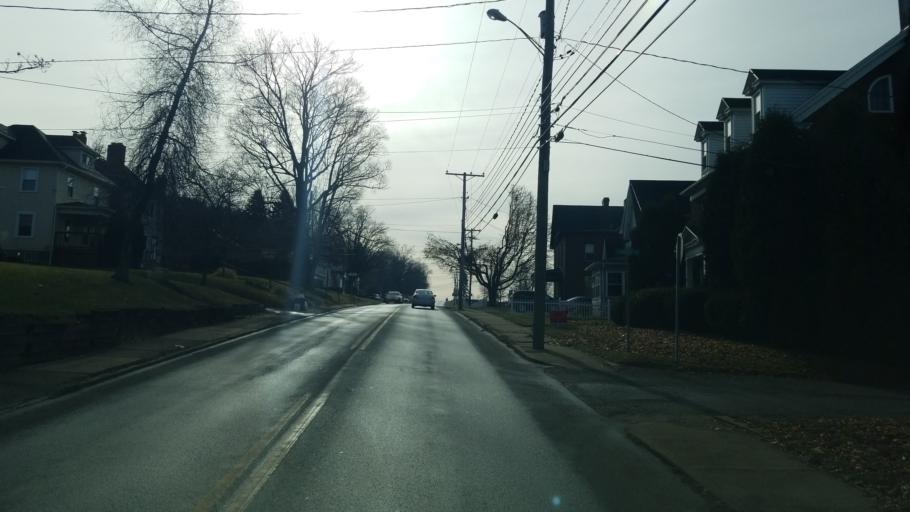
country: US
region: Pennsylvania
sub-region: Indiana County
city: Indiana
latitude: 40.6140
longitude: -79.1505
